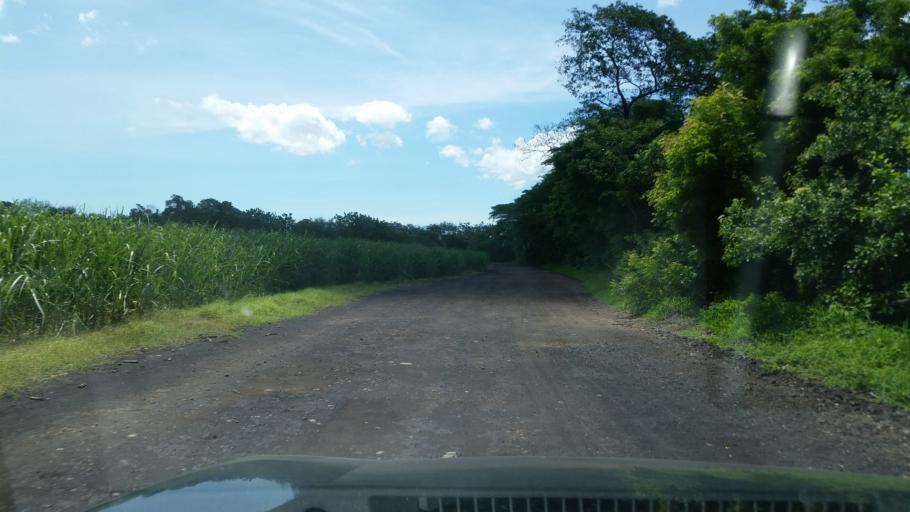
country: NI
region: Chinandega
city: El Viejo
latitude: 12.7459
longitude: -87.1360
